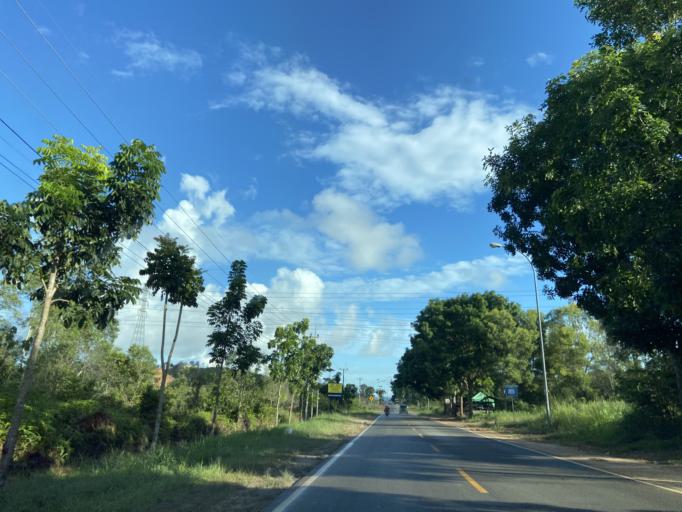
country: SG
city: Singapore
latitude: 1.0174
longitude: 104.0163
